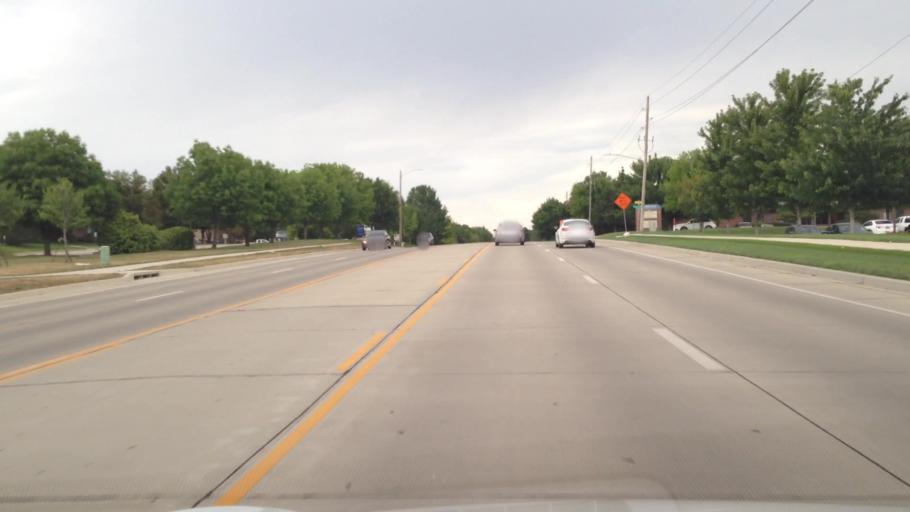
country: US
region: Kansas
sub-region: Douglas County
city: Lawrence
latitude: 38.9594
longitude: -95.3069
